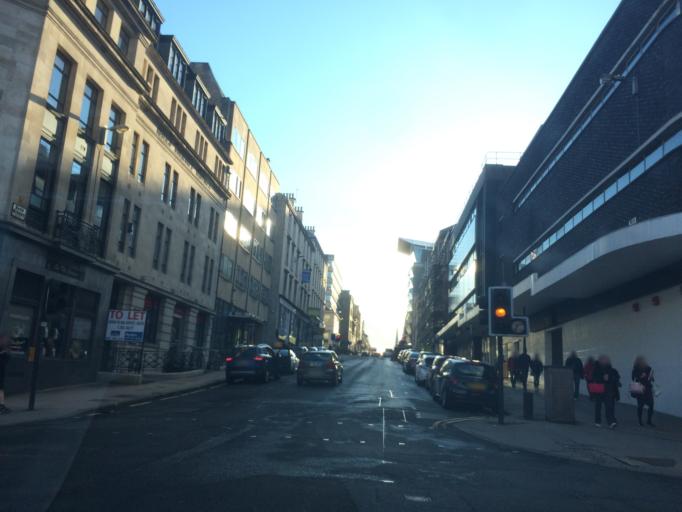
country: GB
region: Scotland
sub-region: Glasgow City
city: Glasgow
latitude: 55.8638
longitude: -4.2557
